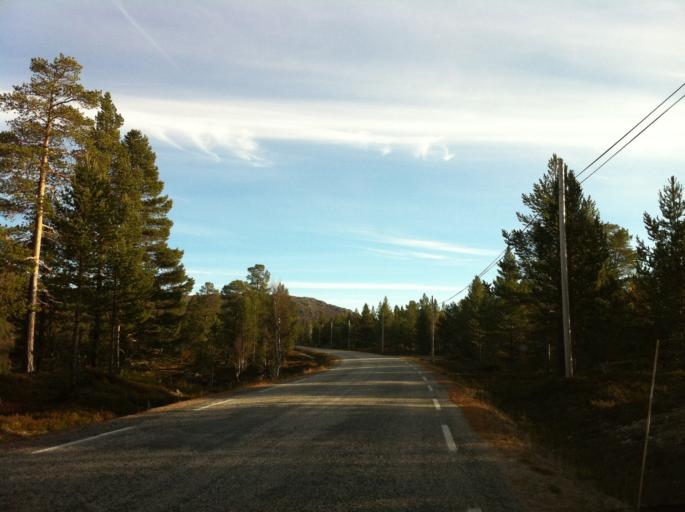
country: NO
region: Hedmark
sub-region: Engerdal
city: Engerdal
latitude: 62.1264
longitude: 11.9992
